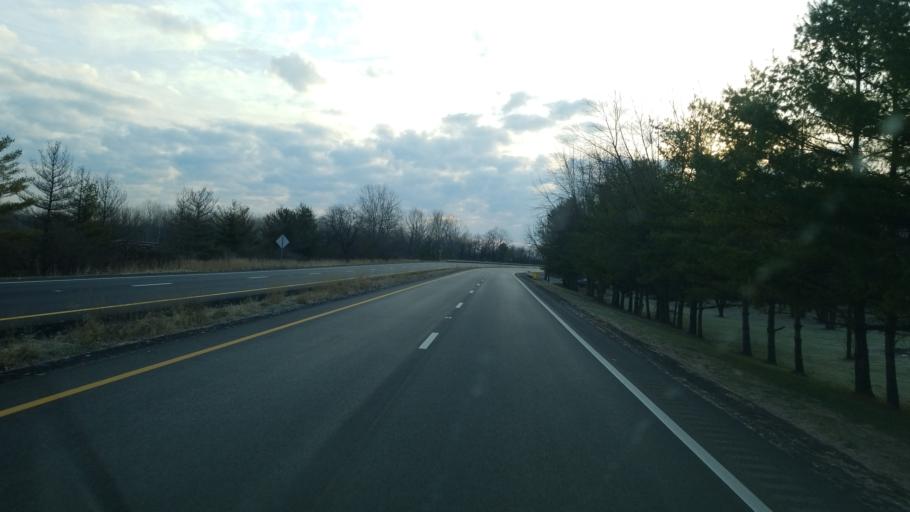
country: US
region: Ohio
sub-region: Ross County
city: Chillicothe
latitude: 39.3197
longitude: -82.9660
